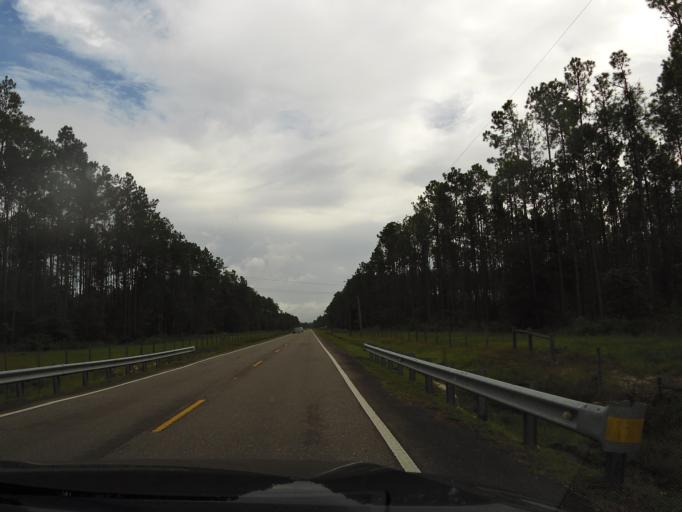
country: US
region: Florida
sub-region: Duval County
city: Baldwin
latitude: 30.3553
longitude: -81.9144
